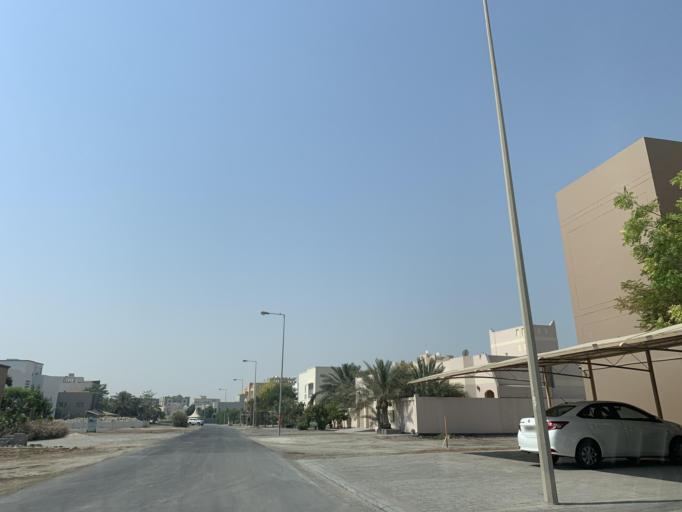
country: BH
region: Manama
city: Jidd Hafs
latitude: 26.1980
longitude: 50.5129
